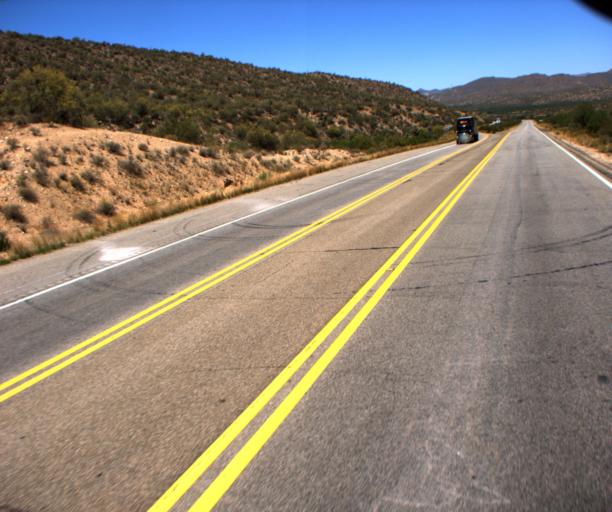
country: US
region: Arizona
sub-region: Yavapai County
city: Bagdad
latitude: 34.3601
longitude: -113.1720
